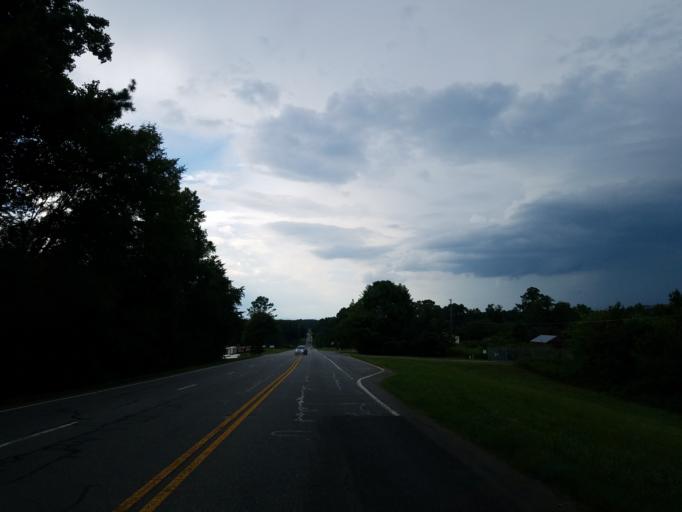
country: US
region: Georgia
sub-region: Bartow County
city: Adairsville
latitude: 34.3309
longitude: -84.9016
